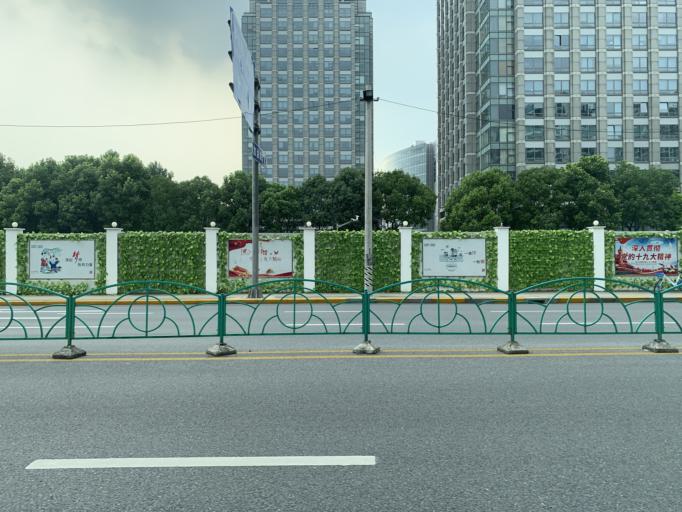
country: CN
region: Shanghai Shi
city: Huamu
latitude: 31.2226
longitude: 121.5475
